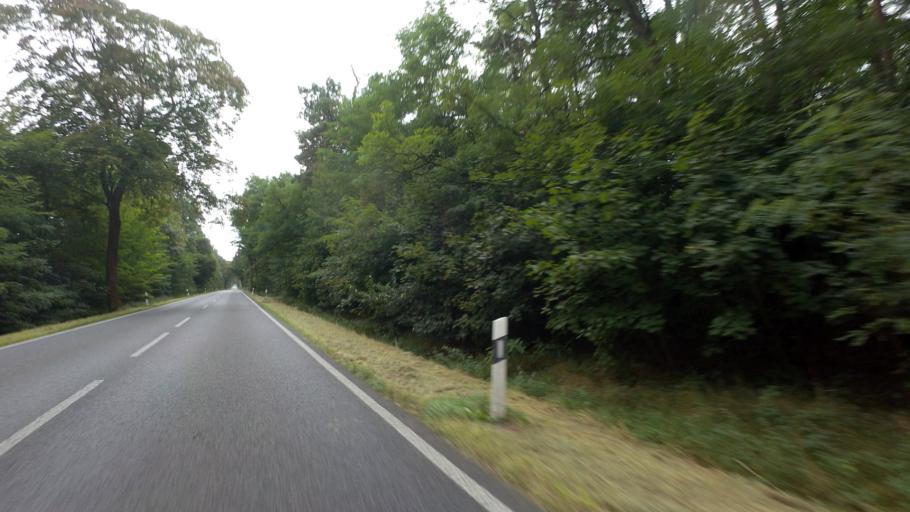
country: DE
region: Brandenburg
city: Baruth
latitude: 52.0926
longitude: 13.4968
